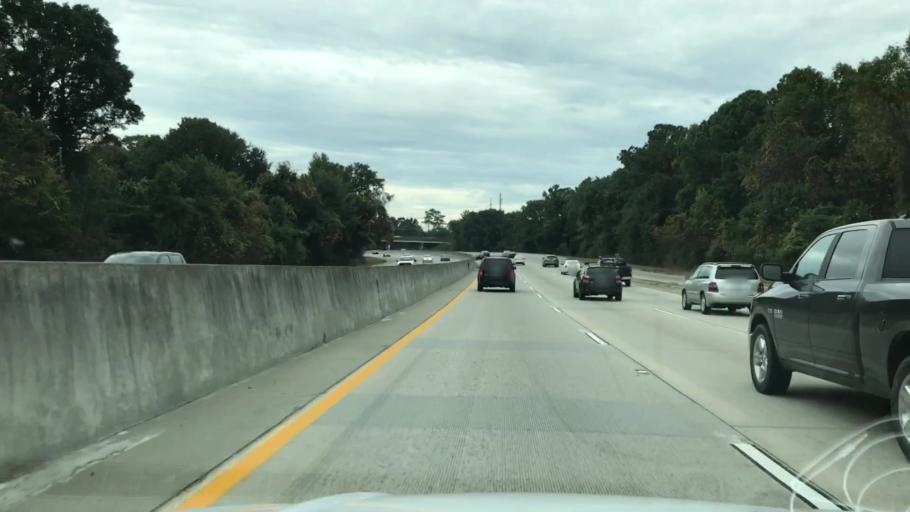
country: US
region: South Carolina
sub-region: Charleston County
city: North Charleston
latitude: 32.8508
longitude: -79.9875
